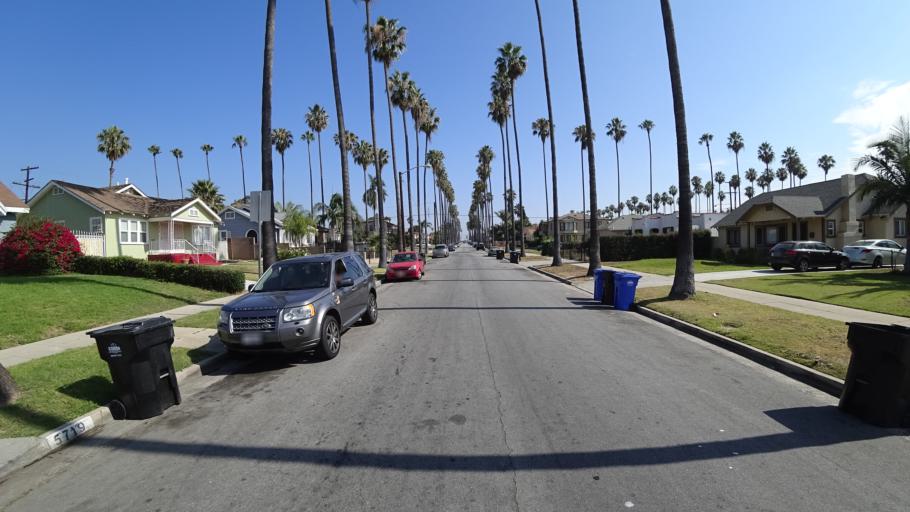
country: US
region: California
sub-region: Los Angeles County
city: View Park-Windsor Hills
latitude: 33.9902
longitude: -118.3420
